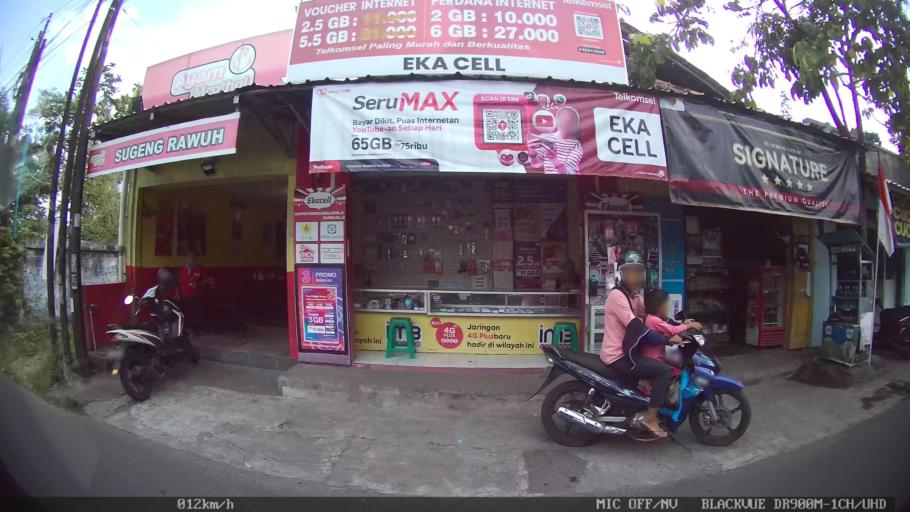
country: ID
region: Daerah Istimewa Yogyakarta
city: Kasihan
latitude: -7.8146
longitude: 110.3327
